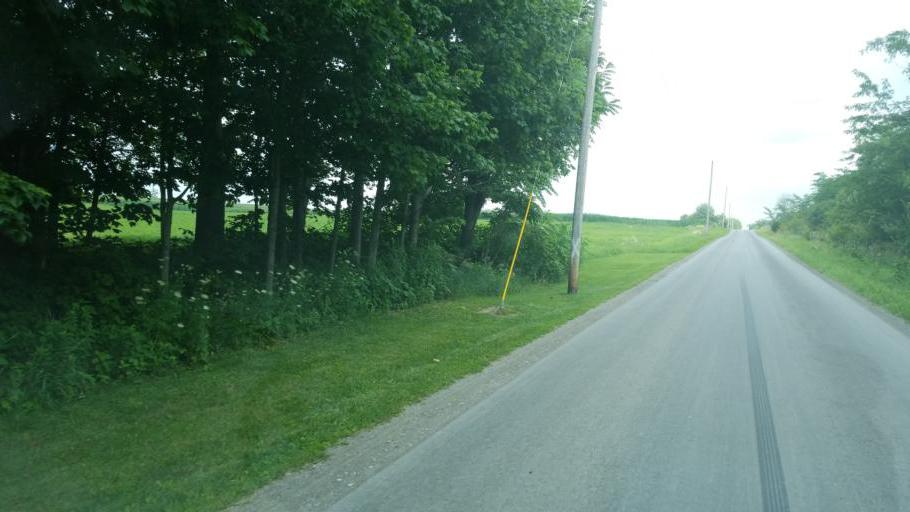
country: US
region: Ohio
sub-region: Hardin County
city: Kenton
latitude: 40.5939
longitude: -83.6169
